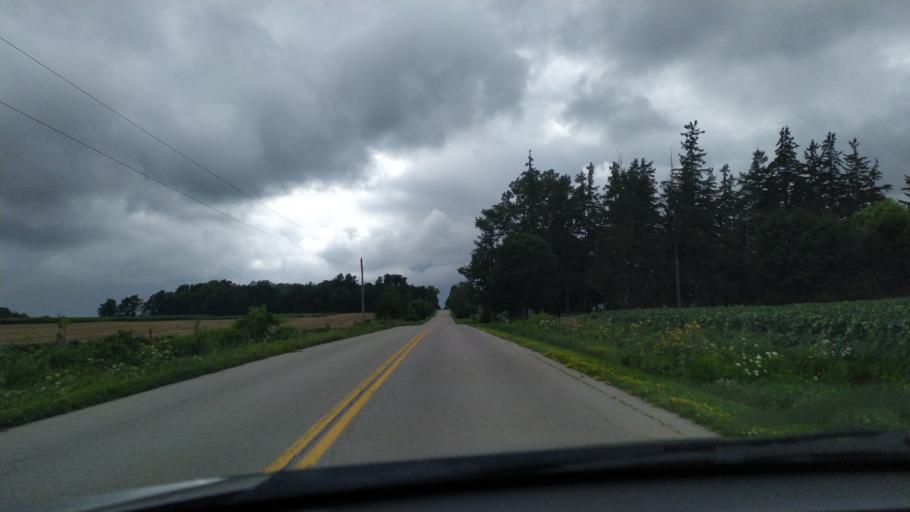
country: CA
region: Ontario
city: Kitchener
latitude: 43.3316
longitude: -80.6541
